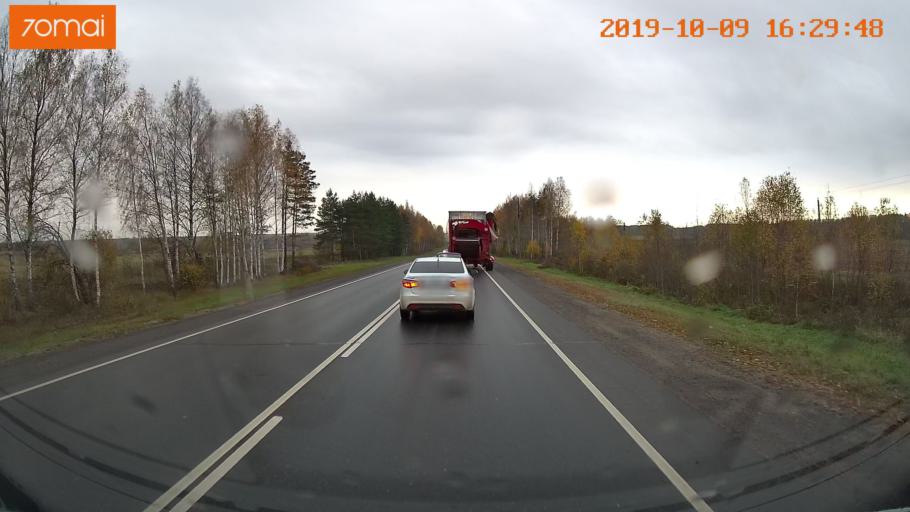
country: RU
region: Kostroma
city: Oktyabr'skiy
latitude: 57.6225
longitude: 40.9374
